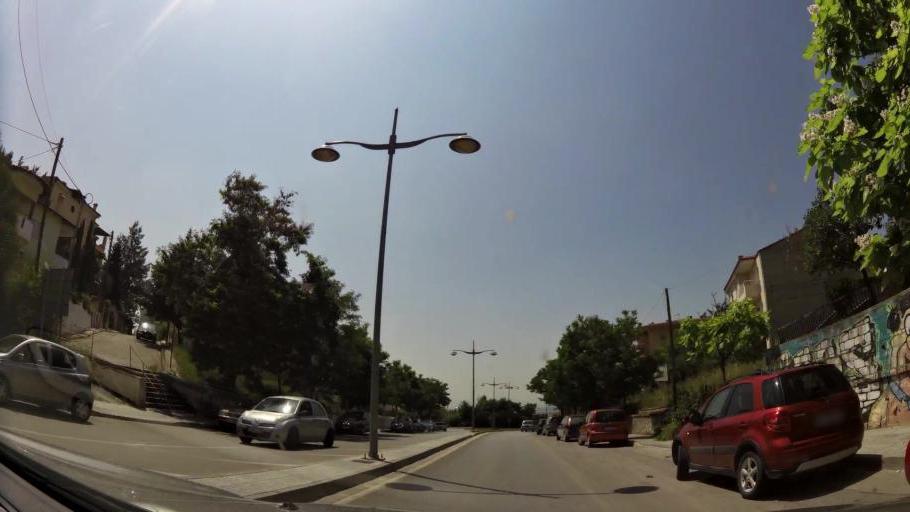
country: GR
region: West Macedonia
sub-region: Nomos Kozanis
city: Kozani
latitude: 40.3100
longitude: 21.7845
